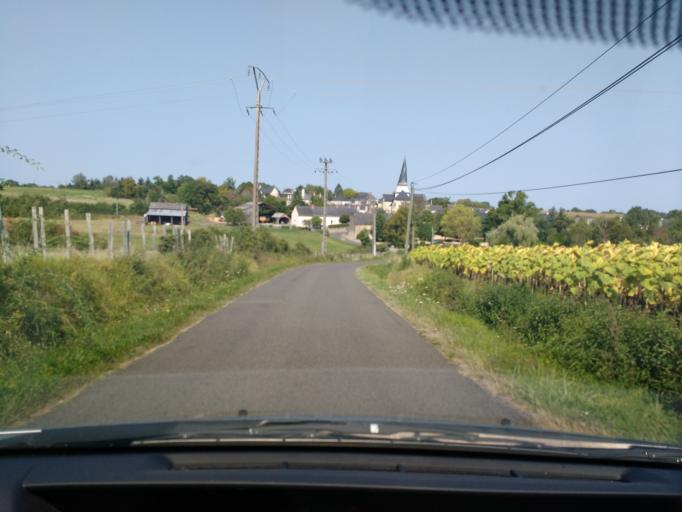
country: FR
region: Pays de la Loire
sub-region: Departement de Maine-et-Loire
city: Bauge-en-Anjou
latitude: 47.5455
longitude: -0.0388
